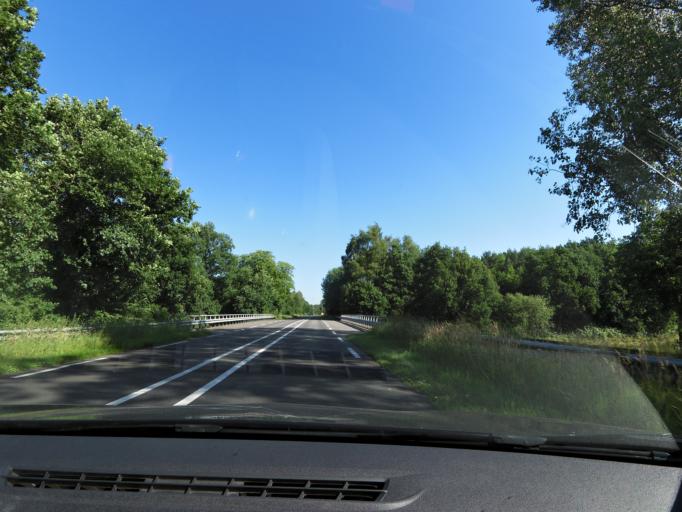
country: NL
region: Overijssel
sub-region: Gemeente Twenterand
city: Den Ham
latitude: 52.4894
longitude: 6.4257
